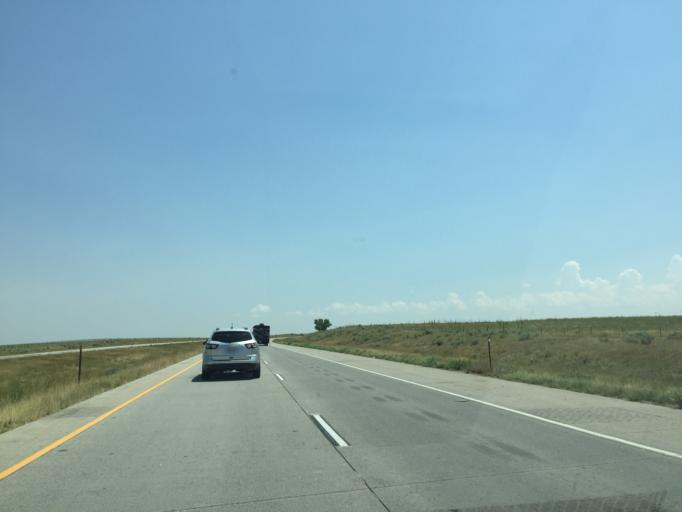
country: US
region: Colorado
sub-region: Arapahoe County
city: Byers
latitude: 39.6667
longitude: -104.0902
